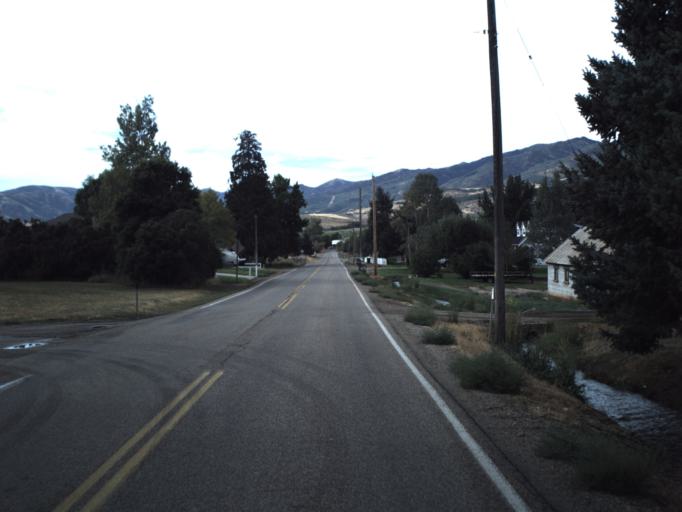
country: US
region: Utah
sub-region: Morgan County
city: Morgan
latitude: 40.9869
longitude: -111.6787
